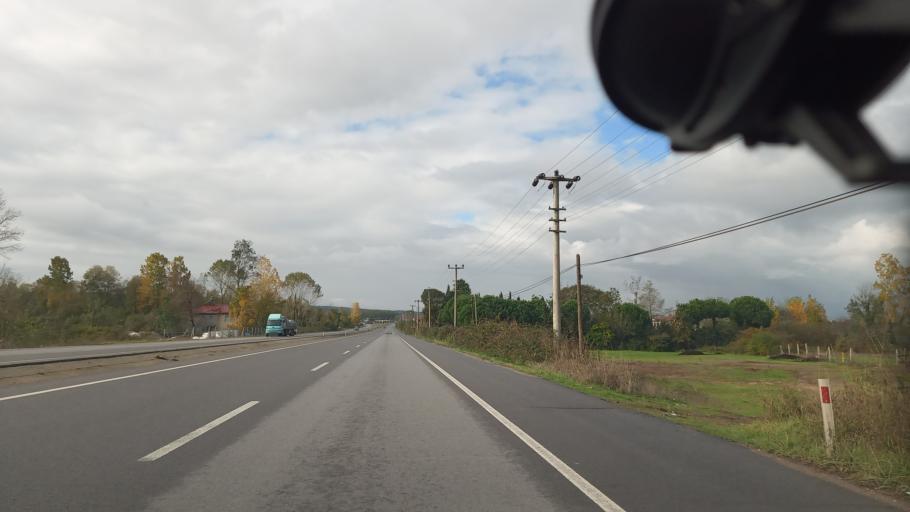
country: TR
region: Sakarya
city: Karasu
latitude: 41.0713
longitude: 30.8125
